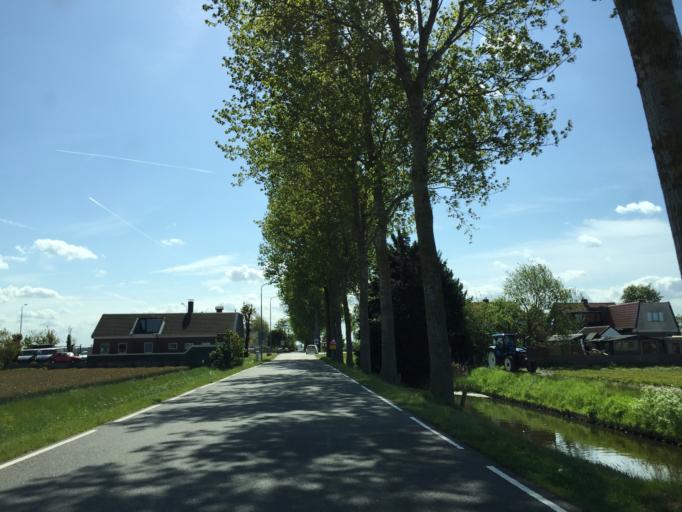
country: NL
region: North Holland
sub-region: Gemeente Haarlemmermeer
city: Hoofddorp
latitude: 52.3388
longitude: 4.6983
